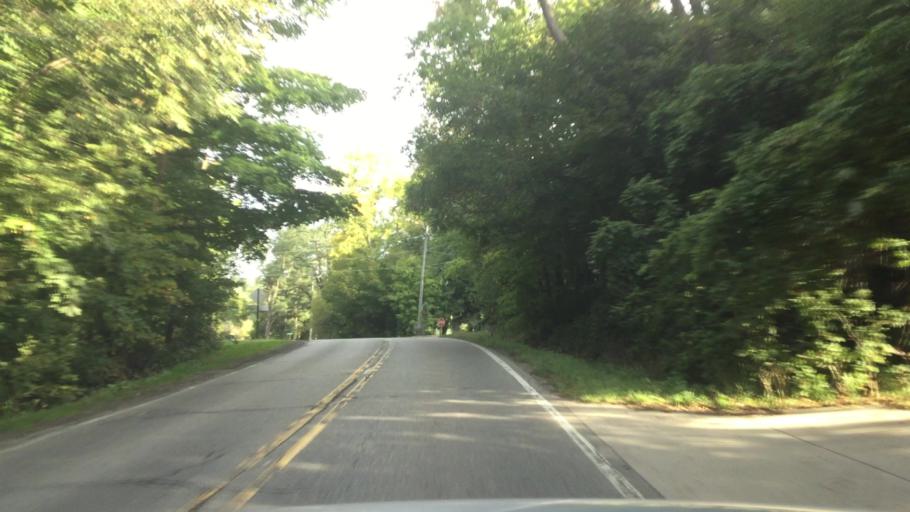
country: US
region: Michigan
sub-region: Livingston County
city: Brighton
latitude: 42.4724
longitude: -83.8338
